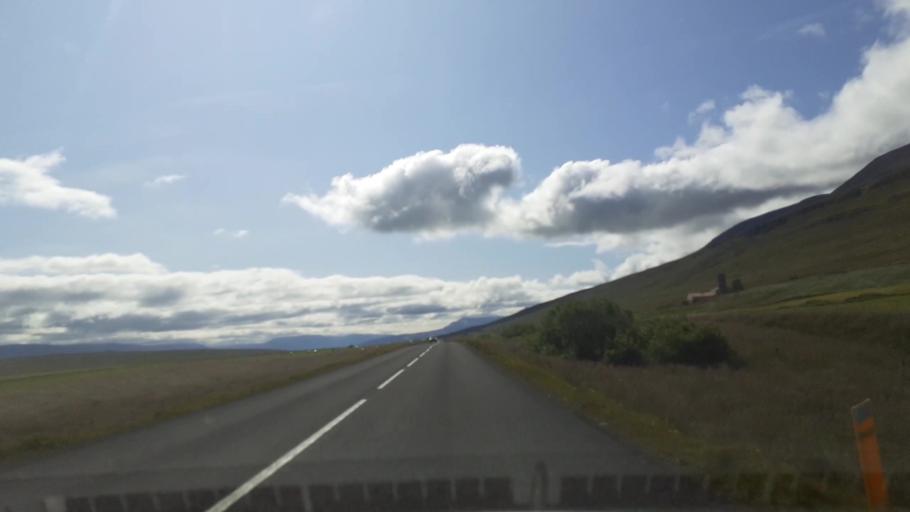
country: IS
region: Northeast
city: Akureyri
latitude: 65.8610
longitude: -18.2603
